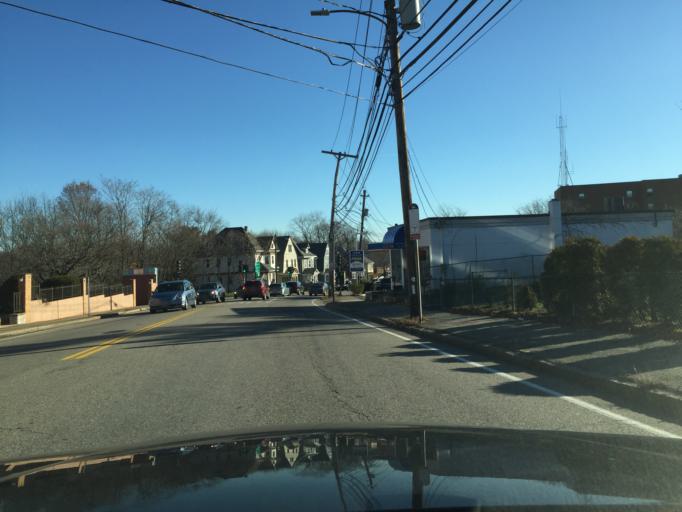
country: US
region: Massachusetts
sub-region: Middlesex County
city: Arlington
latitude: 42.4203
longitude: -71.1530
